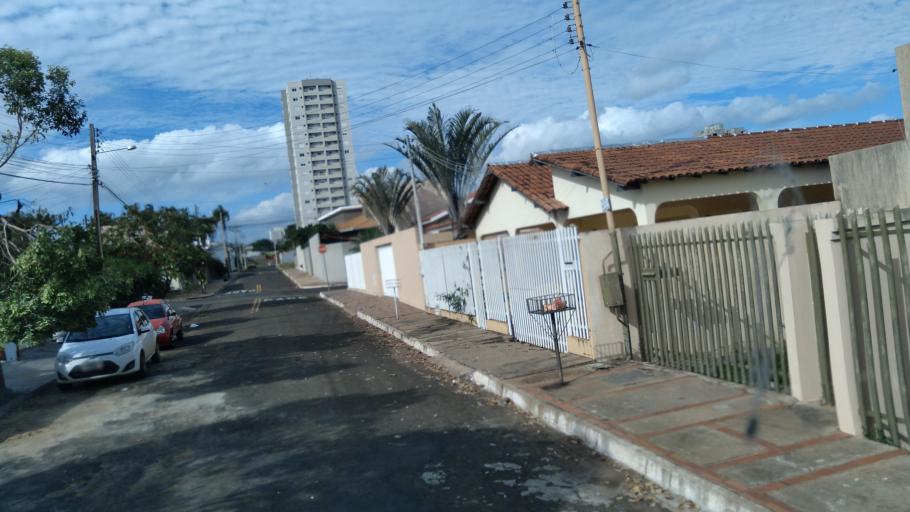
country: BR
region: Goias
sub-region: Mineiros
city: Mineiros
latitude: -17.5620
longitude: -52.5644
